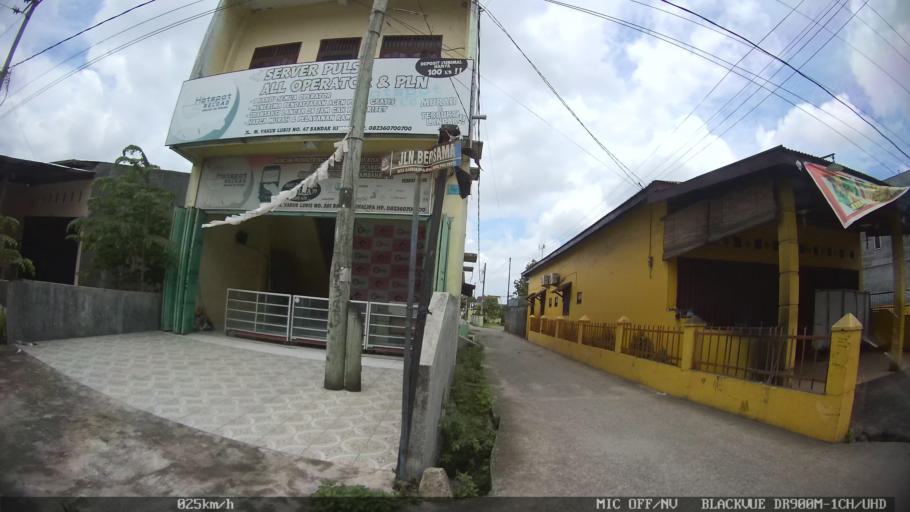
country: ID
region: North Sumatra
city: Medan
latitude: 3.6166
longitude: 98.7481
